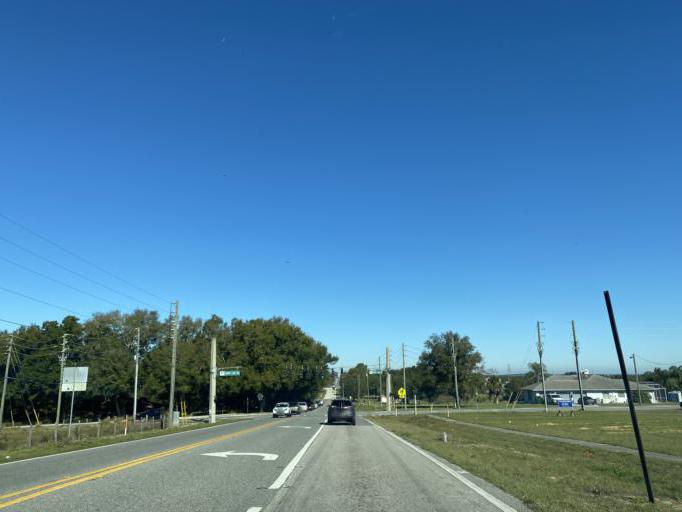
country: US
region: Florida
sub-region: Lake County
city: Minneola
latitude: 28.5244
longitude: -81.7068
